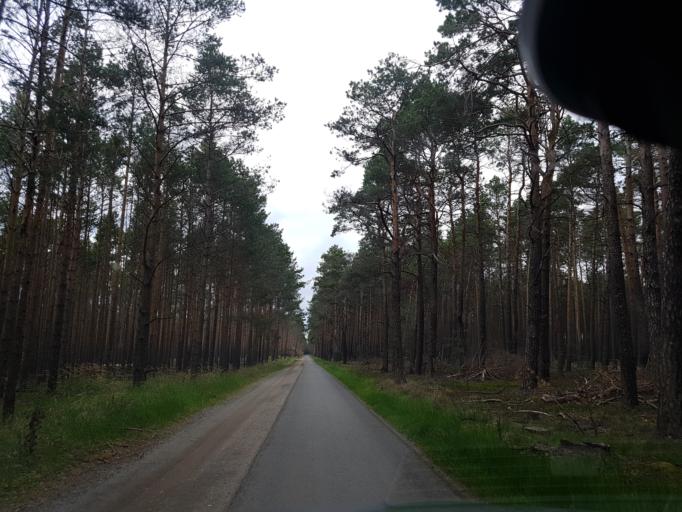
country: DE
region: Brandenburg
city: Crinitz
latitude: 51.6745
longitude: 13.7815
